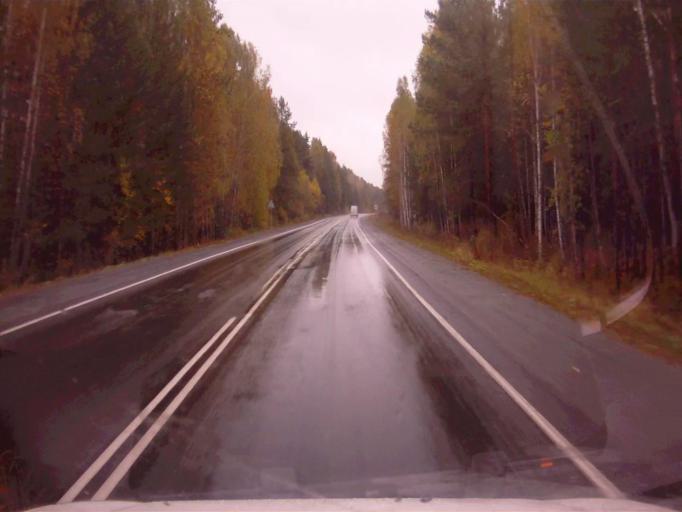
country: RU
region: Chelyabinsk
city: Tayginka
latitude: 55.5579
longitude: 60.6464
